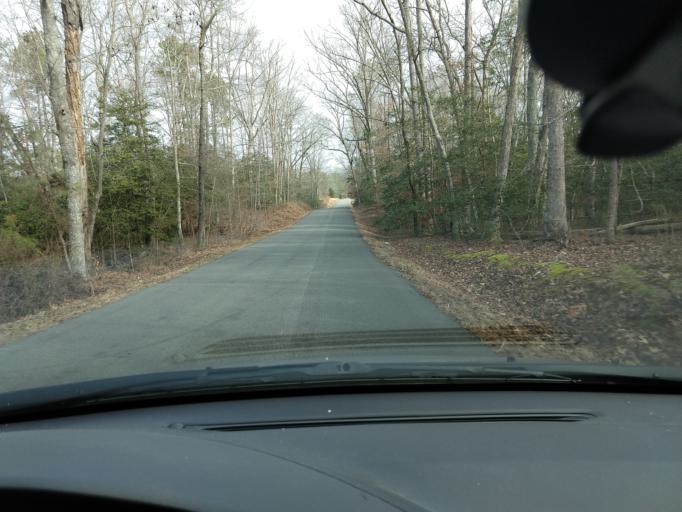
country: US
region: Virginia
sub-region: Henrico County
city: Fort Lee
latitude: 37.4400
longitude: -77.2526
